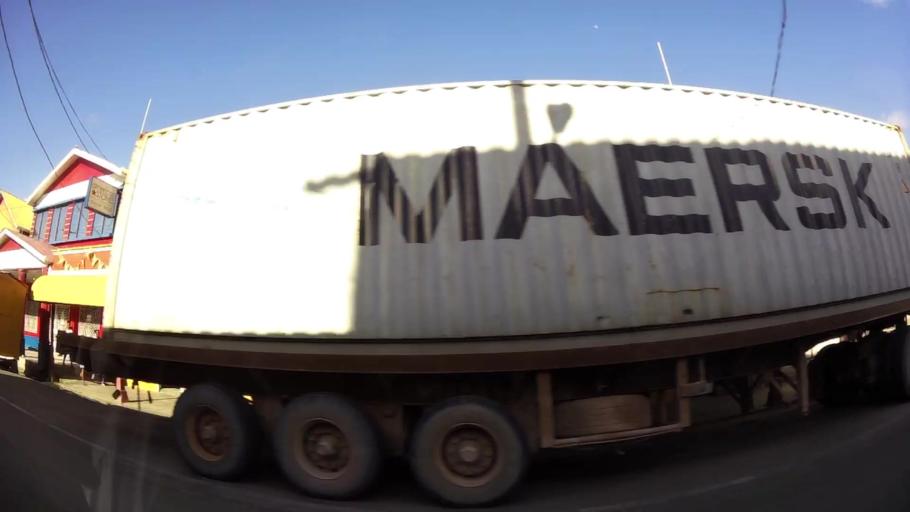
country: GY
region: Demerara-Mahaica
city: Georgetown
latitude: 6.8159
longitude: -58.1663
